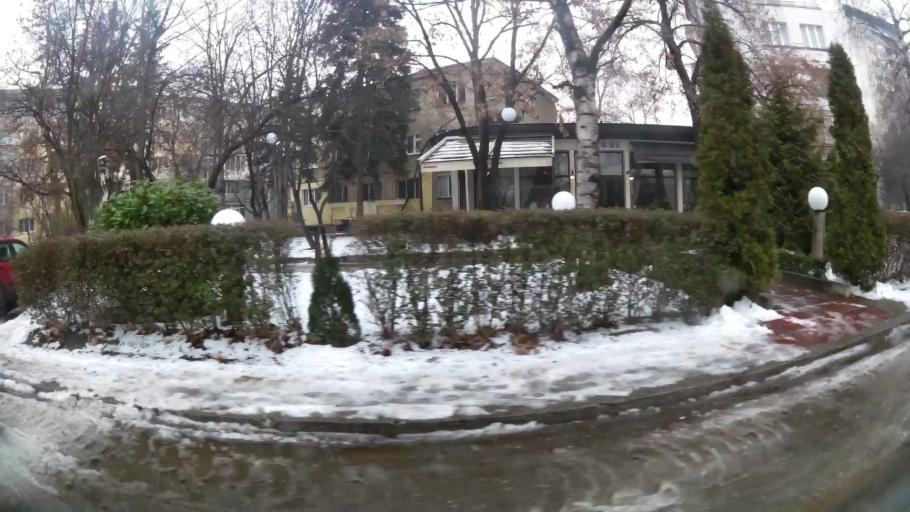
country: BG
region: Sofia-Capital
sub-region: Stolichna Obshtina
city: Sofia
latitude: 42.6820
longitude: 23.2935
